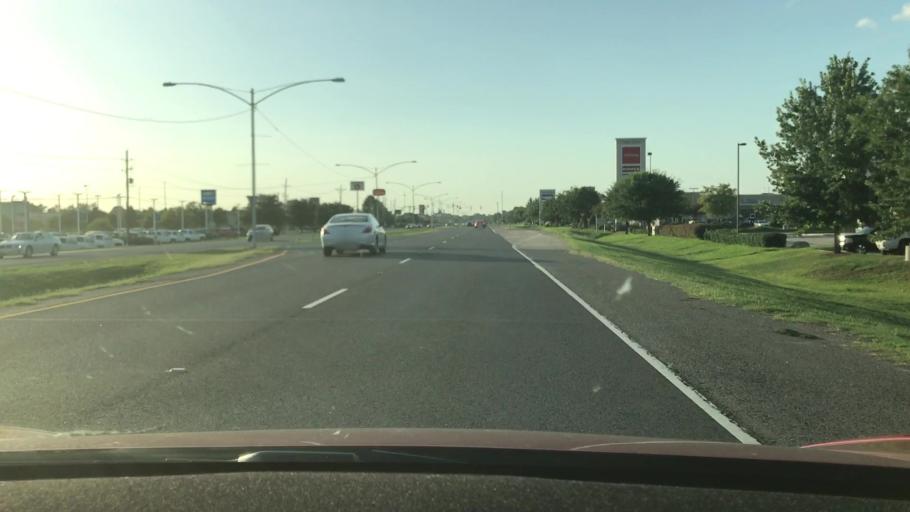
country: US
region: Louisiana
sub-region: Bossier Parish
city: Bossier City
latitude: 32.4361
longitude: -93.7142
